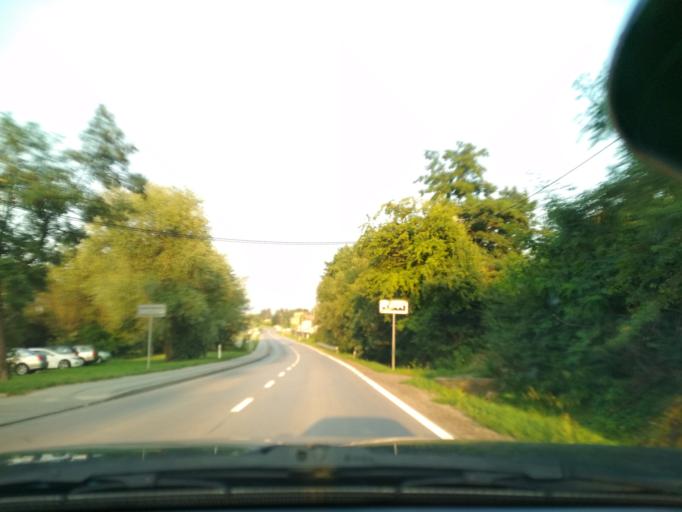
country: PL
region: Lesser Poland Voivodeship
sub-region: Powiat olkuski
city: Wolbrom
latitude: 50.3915
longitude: 19.7506
